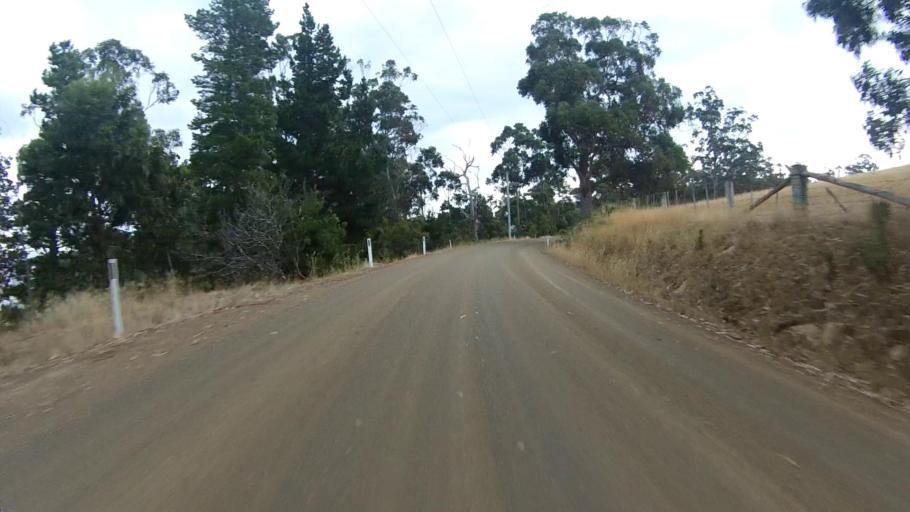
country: AU
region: Tasmania
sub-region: Huon Valley
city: Cygnet
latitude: -43.2368
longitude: 147.0991
